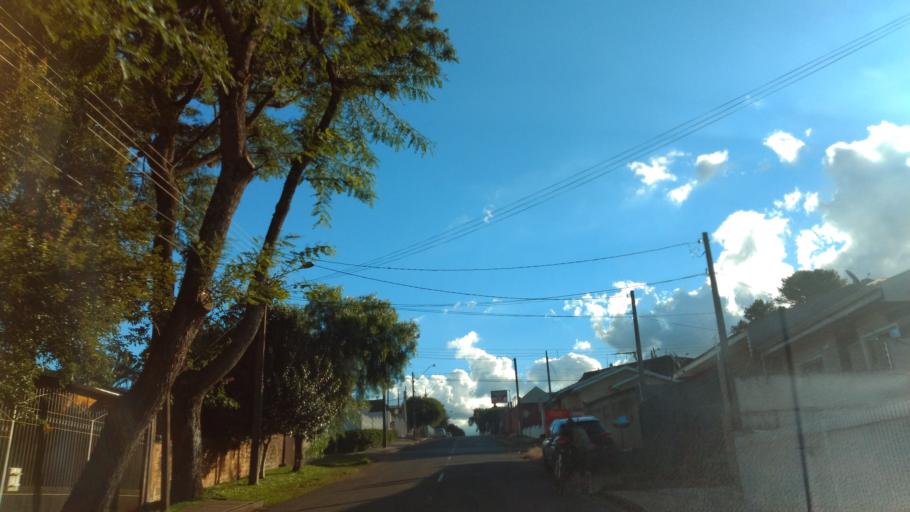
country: BR
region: Parana
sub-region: Guarapuava
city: Guarapuava
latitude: -25.3837
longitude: -51.4589
